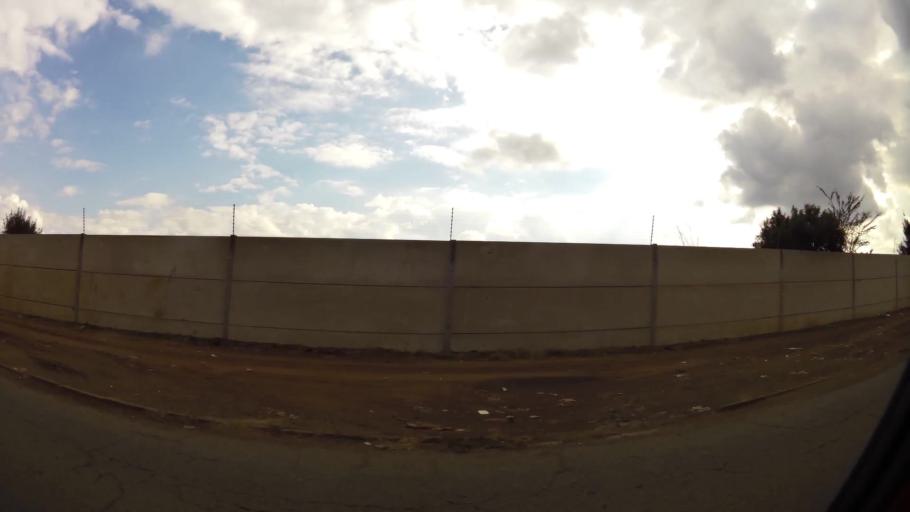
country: ZA
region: Gauteng
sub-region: Sedibeng District Municipality
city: Vanderbijlpark
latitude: -26.6756
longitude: 27.8181
